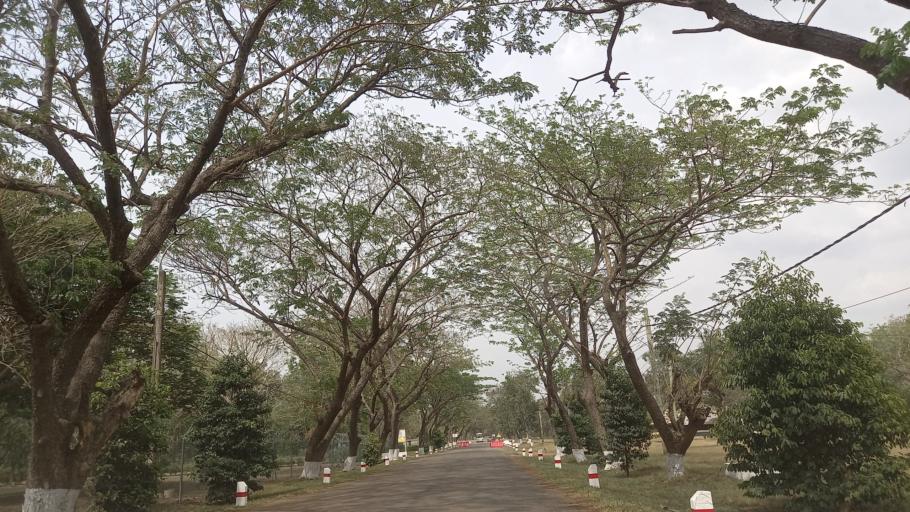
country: GH
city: Akropong
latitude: 6.0934
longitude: 0.1140
